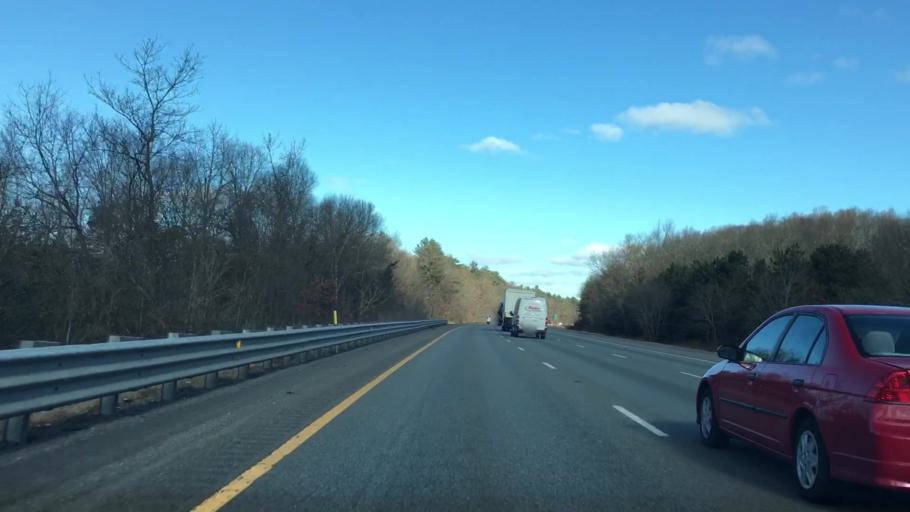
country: US
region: Massachusetts
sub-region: Worcester County
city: Bolton
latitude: 42.4035
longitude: -71.6082
